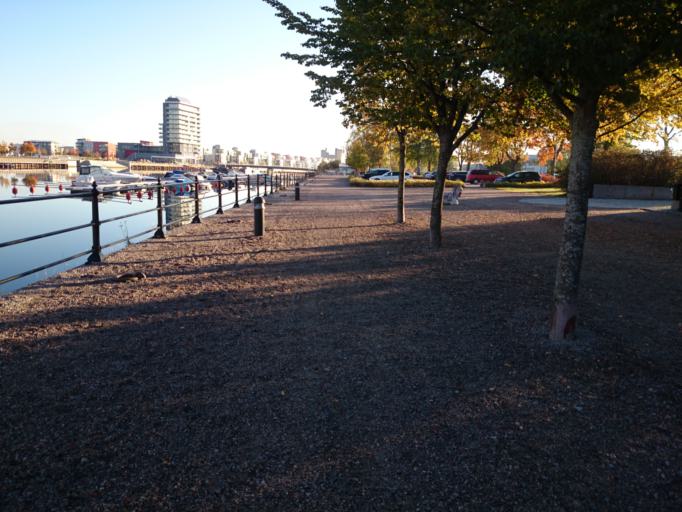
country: SE
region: Gaevleborg
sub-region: Gavle Kommun
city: Gavle
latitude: 60.6763
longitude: 17.1583
